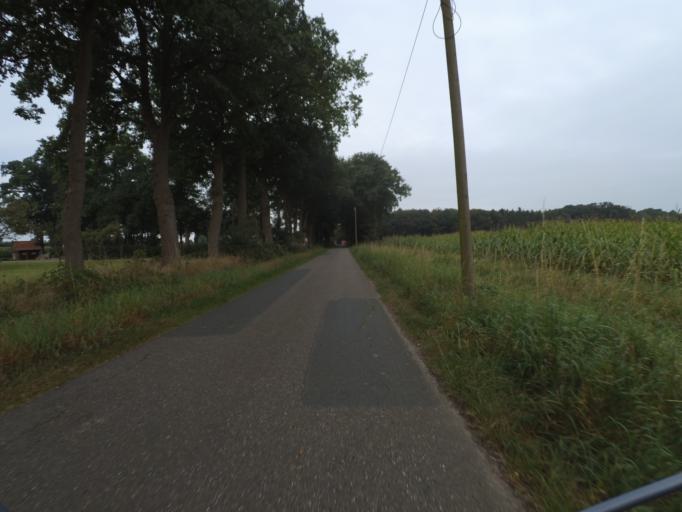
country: DE
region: Lower Saxony
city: Isterberg
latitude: 52.3302
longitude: 7.0700
